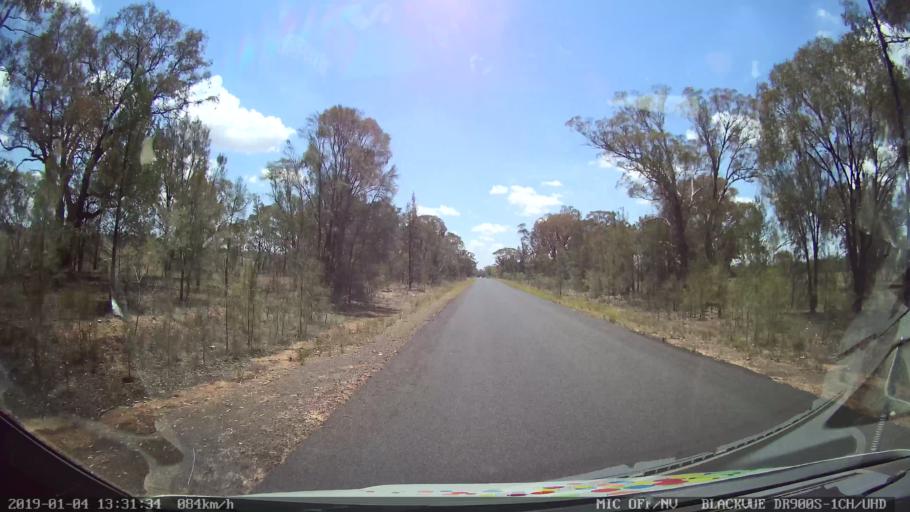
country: AU
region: New South Wales
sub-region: Parkes
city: Peak Hill
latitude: -32.6211
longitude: 148.5487
